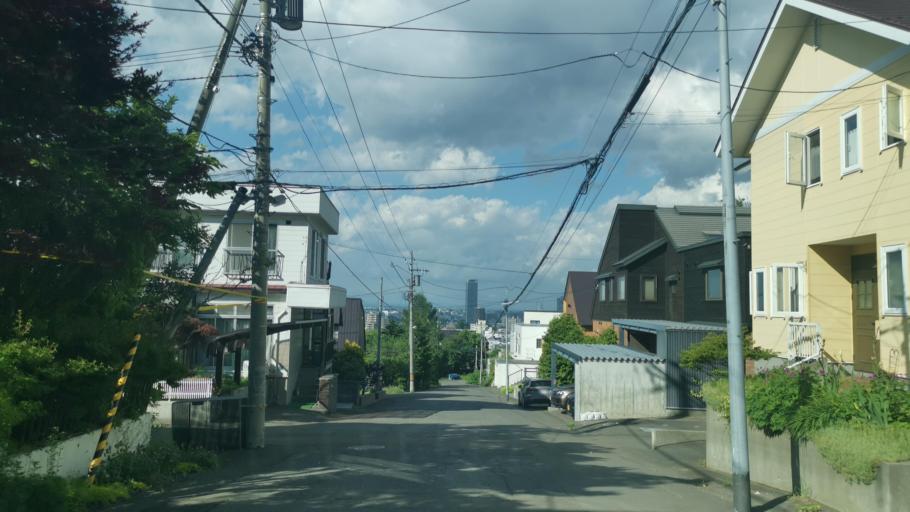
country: JP
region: Hokkaido
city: Sapporo
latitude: 43.0693
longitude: 141.2843
